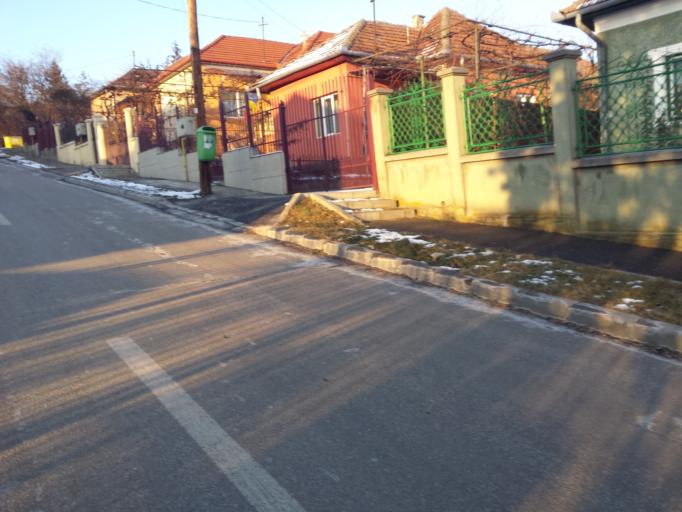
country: RO
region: Cluj
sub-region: Municipiul Cluj-Napoca
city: Cluj-Napoca
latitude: 46.7915
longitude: 23.5864
